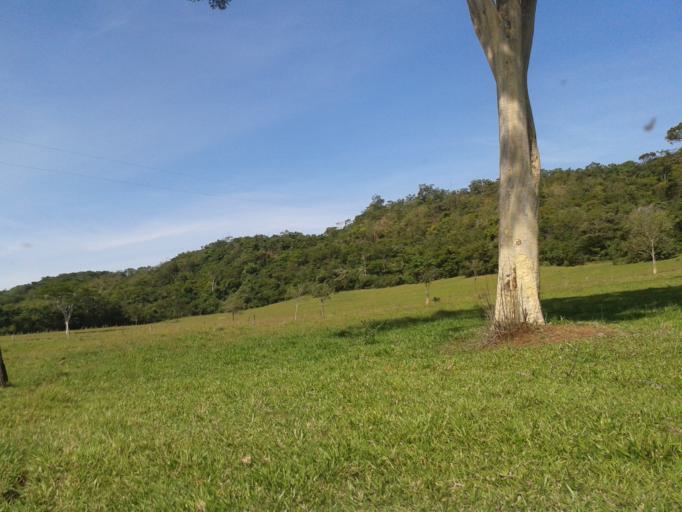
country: BR
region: Minas Gerais
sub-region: Campina Verde
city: Campina Verde
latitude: -19.4441
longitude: -49.6866
